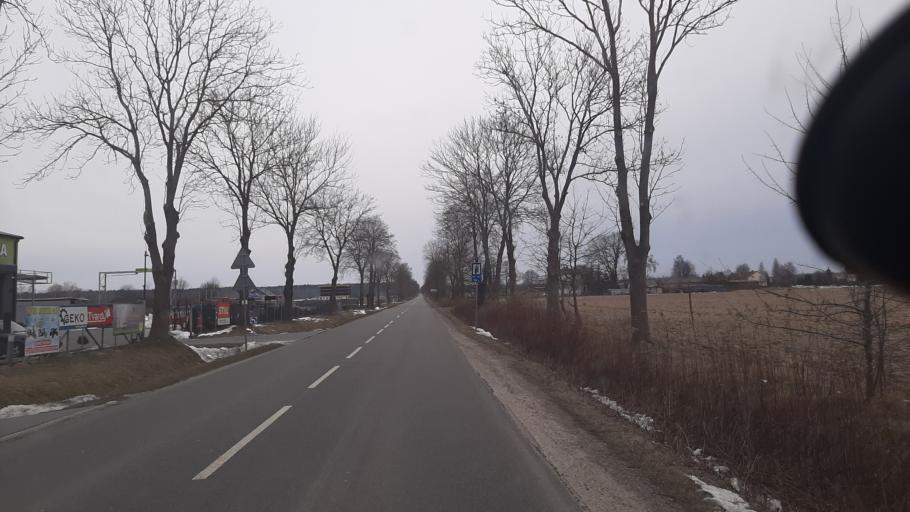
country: PL
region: Lublin Voivodeship
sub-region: Powiat lubartowski
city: Kamionka
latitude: 51.4922
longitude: 22.4309
